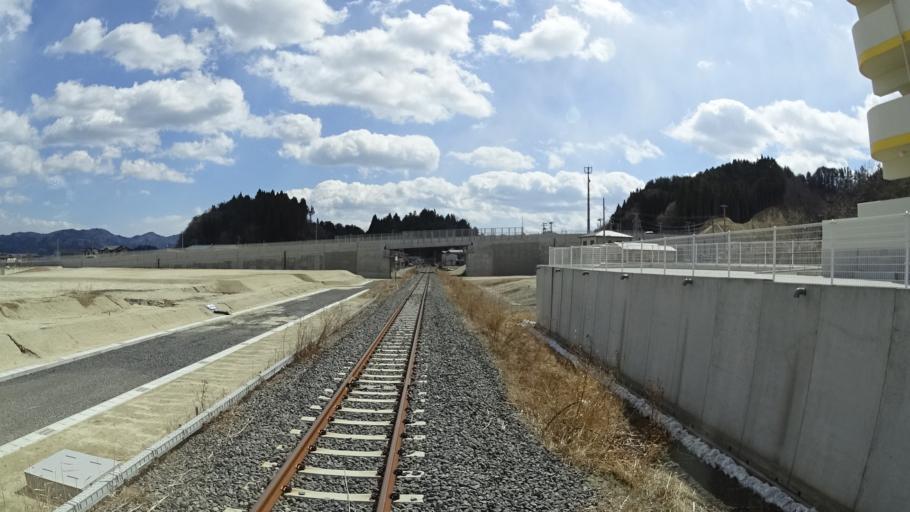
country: JP
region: Iwate
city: Yamada
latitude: 39.4739
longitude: 141.9474
